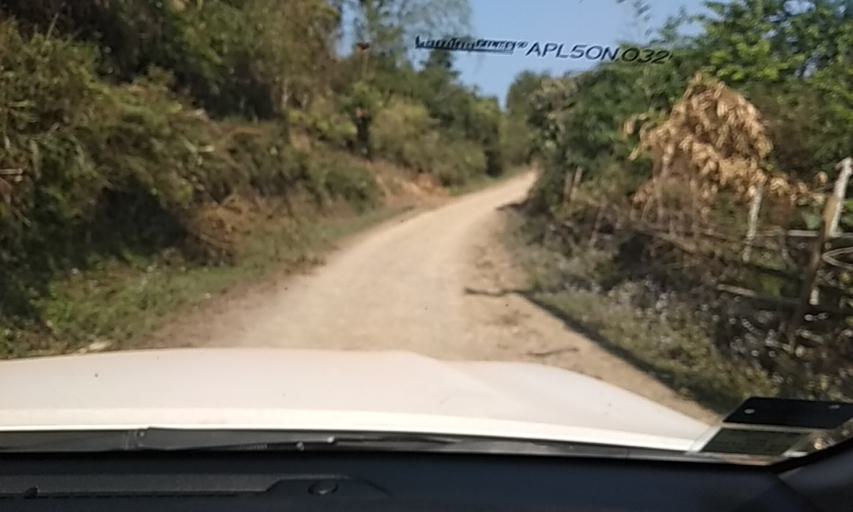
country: LA
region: Phongsali
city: Phongsali
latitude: 21.6970
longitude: 102.0826
